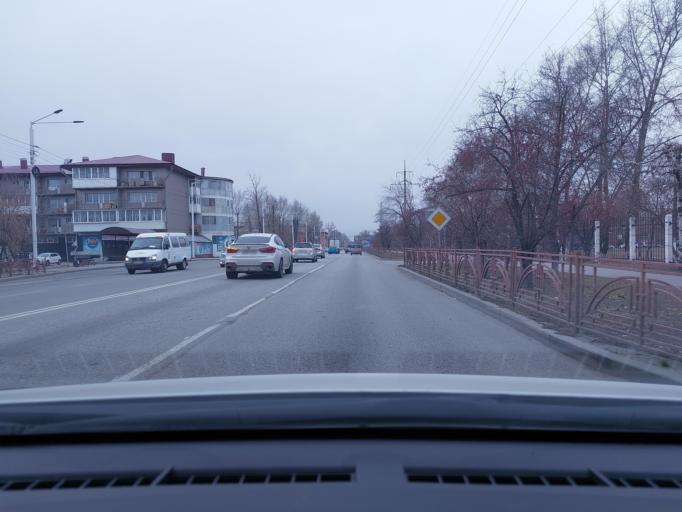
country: RU
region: Irkutsk
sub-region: Irkutskiy Rayon
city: Irkutsk
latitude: 52.3403
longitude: 104.2299
